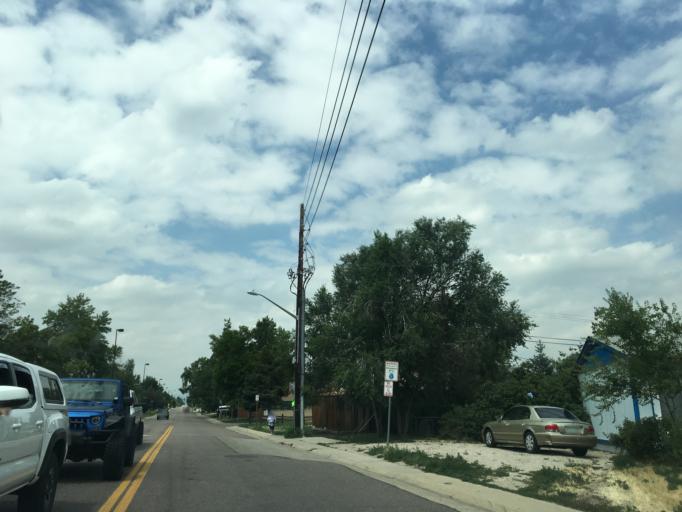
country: US
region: Colorado
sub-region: Arapahoe County
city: Sheridan
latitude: 39.6677
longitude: -105.0253
